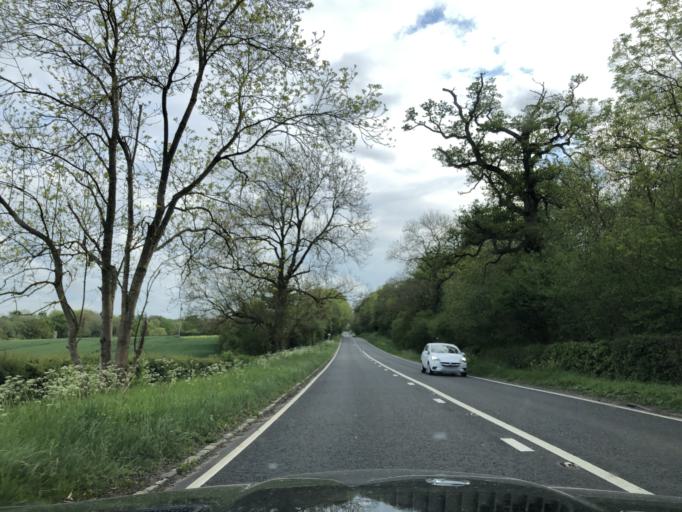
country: GB
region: England
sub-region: Gloucestershire
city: Moreton in Marsh
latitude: 52.0100
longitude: -1.6930
